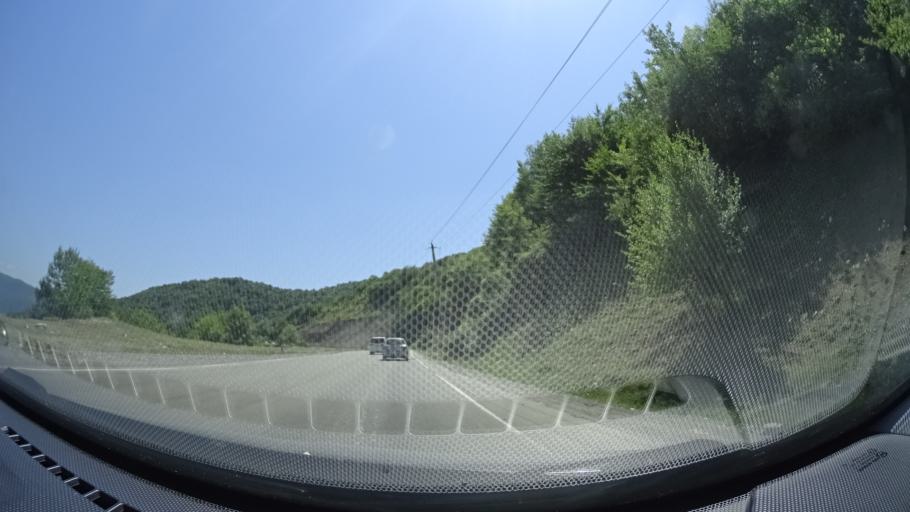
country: GE
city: Zhinvali
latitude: 42.1567
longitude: 44.7181
